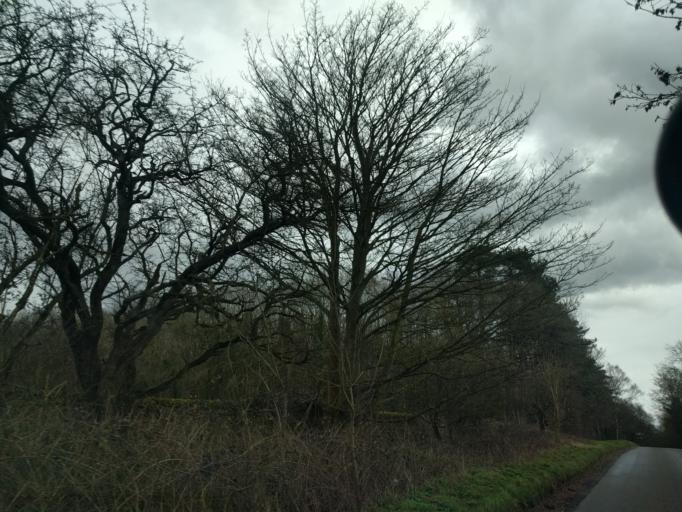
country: GB
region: England
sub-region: Gloucestershire
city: Tetbury
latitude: 51.6232
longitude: -2.2175
